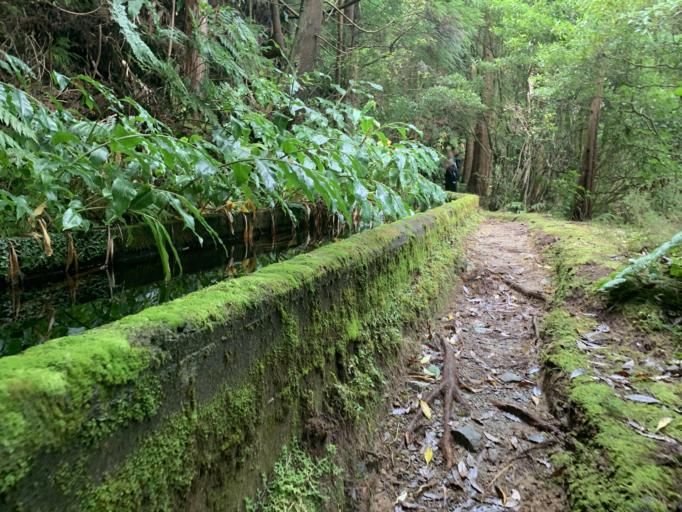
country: PT
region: Azores
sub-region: Vila Franca do Campo
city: Vila Franca do Campo
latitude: 37.7451
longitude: -25.4759
